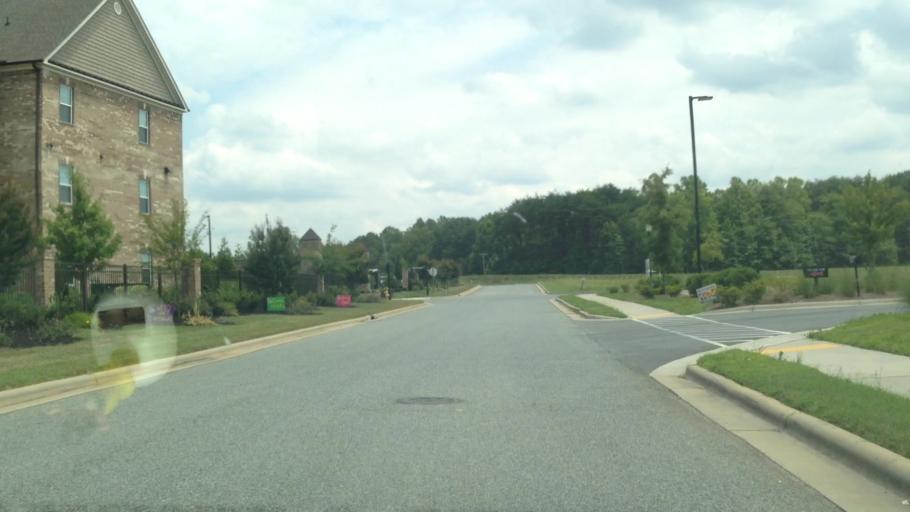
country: US
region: North Carolina
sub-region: Forsyth County
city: Walkertown
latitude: 36.1649
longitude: -80.1344
